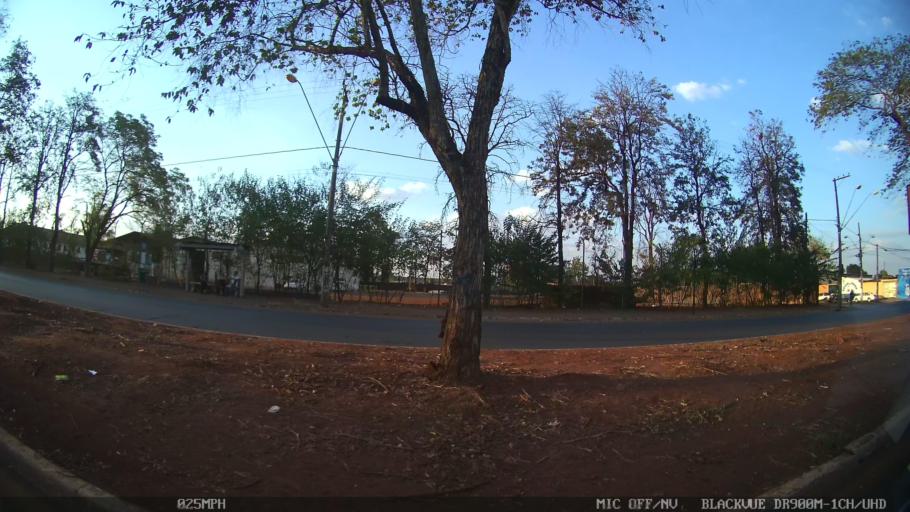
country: BR
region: Sao Paulo
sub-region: Ribeirao Preto
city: Ribeirao Preto
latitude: -21.1465
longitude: -47.7678
